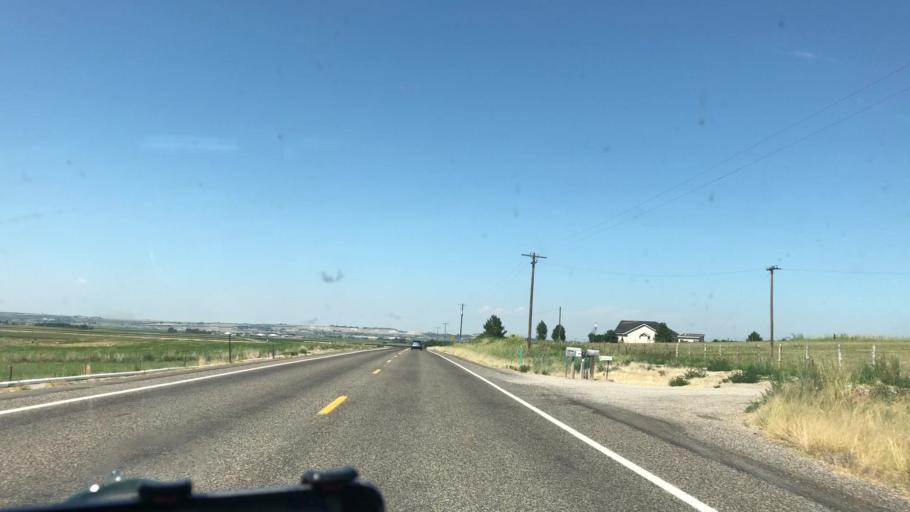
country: US
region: Idaho
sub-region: Owyhee County
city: Marsing
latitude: 43.5175
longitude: -116.8531
